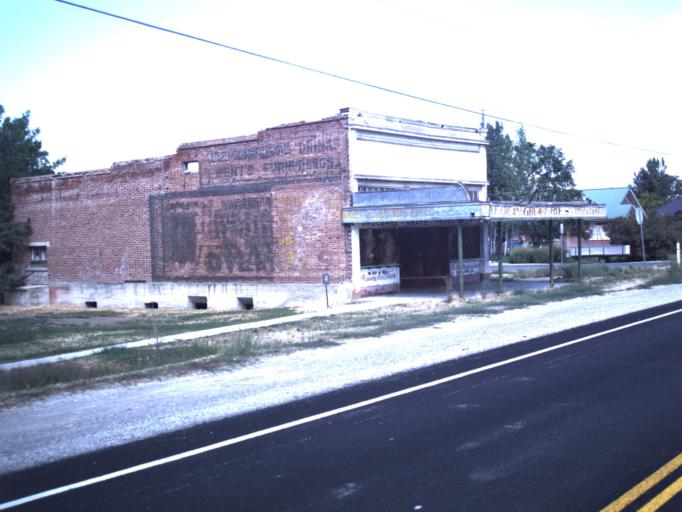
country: US
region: Utah
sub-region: Box Elder County
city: Honeyville
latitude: 41.6140
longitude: -112.1270
